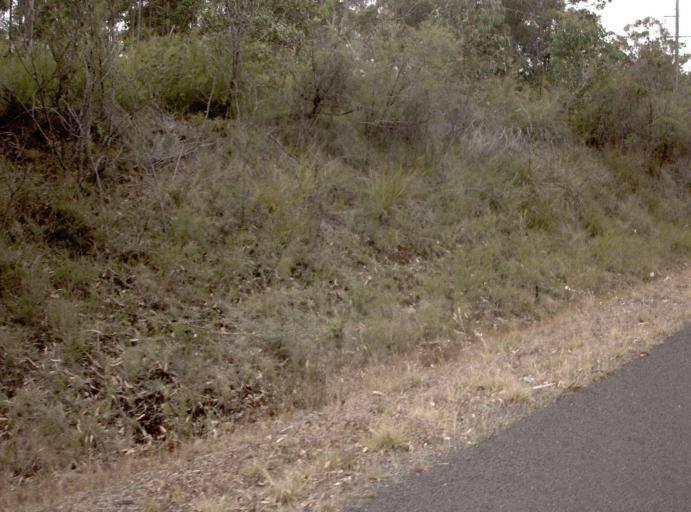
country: AU
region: Victoria
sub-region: East Gippsland
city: Lakes Entrance
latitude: -37.7291
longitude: 147.9317
